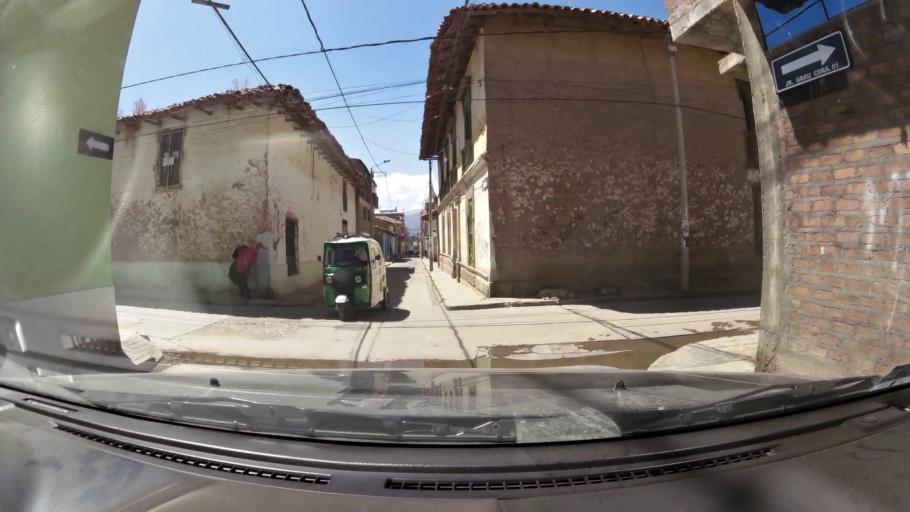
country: PE
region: Junin
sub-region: Provincia de Jauja
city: Jauja
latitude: -11.7758
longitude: -75.5022
